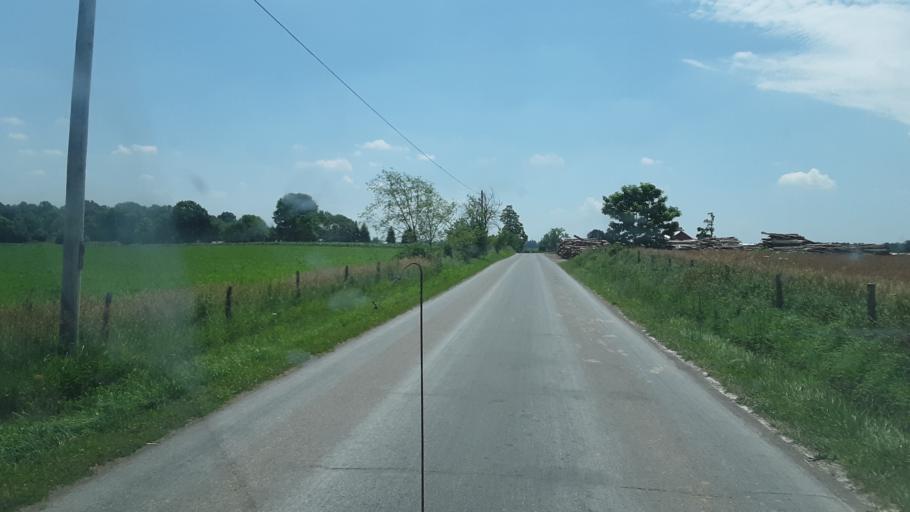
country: US
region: Ohio
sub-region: Wayne County
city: Apple Creek
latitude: 40.7076
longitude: -81.7682
